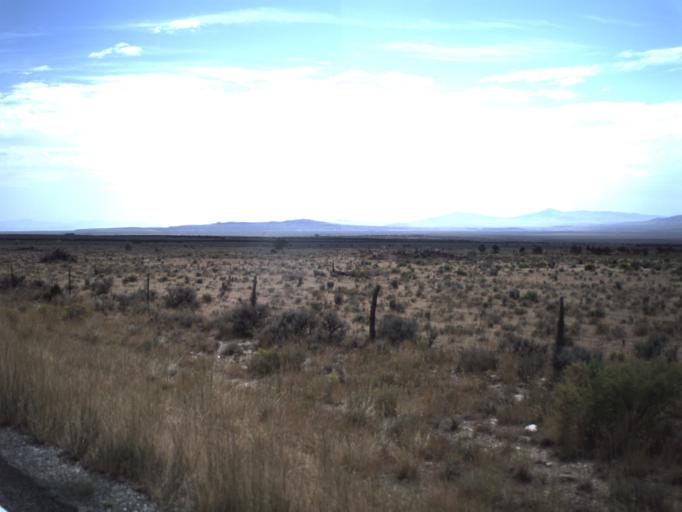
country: US
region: Idaho
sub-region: Cassia County
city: Burley
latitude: 41.8185
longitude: -113.3986
